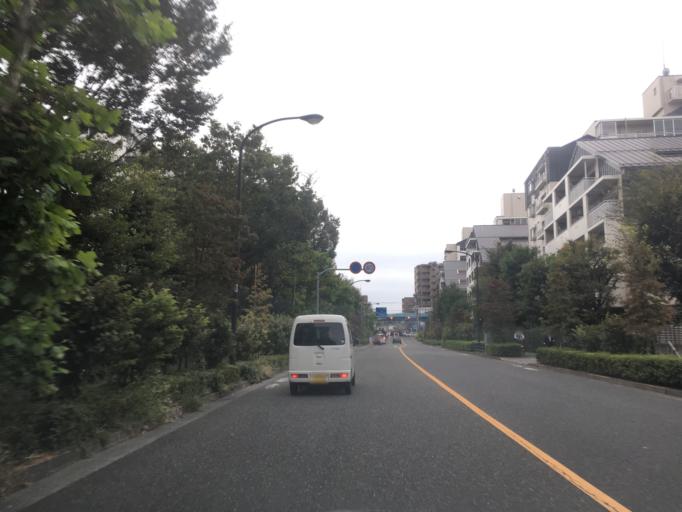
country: JP
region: Tokyo
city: Kokubunji
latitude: 35.6973
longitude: 139.4670
